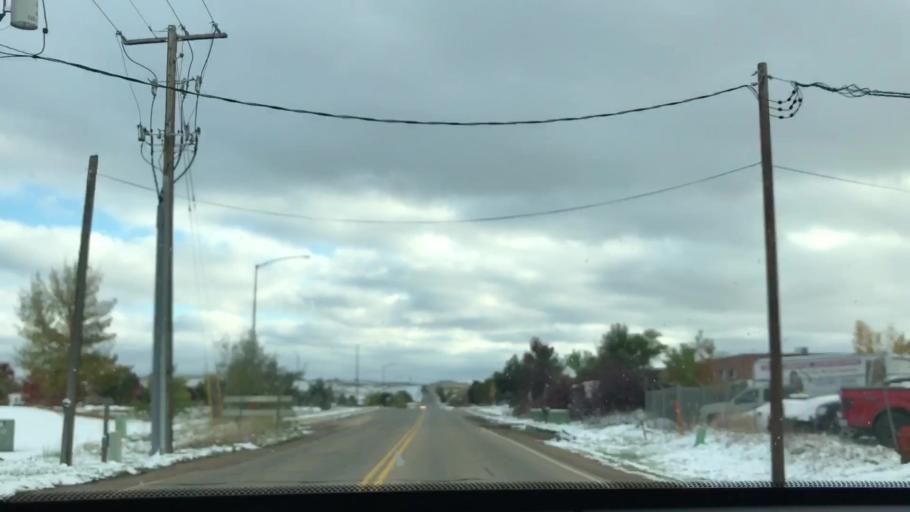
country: US
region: Colorado
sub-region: Boulder County
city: Lafayette
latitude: 39.9816
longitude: -105.0719
